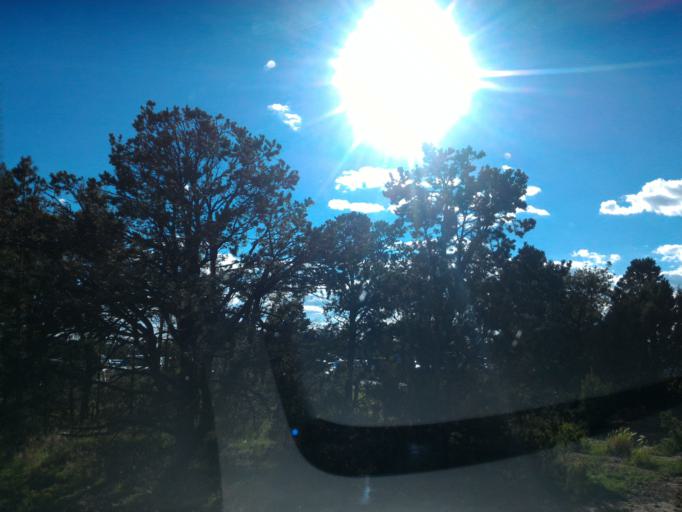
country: US
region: Arizona
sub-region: Coconino County
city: Grand Canyon
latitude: 36.0585
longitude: -112.1067
